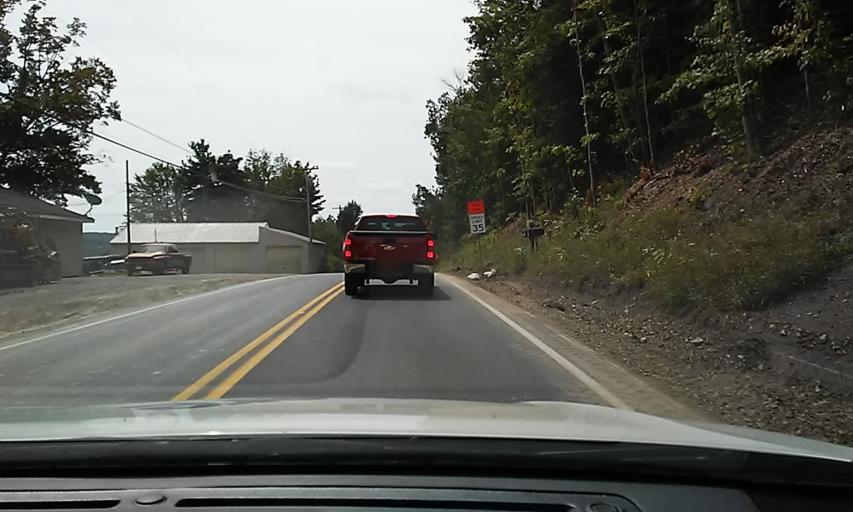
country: US
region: Pennsylvania
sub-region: Clearfield County
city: Treasure Lake
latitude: 41.1729
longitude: -78.6510
